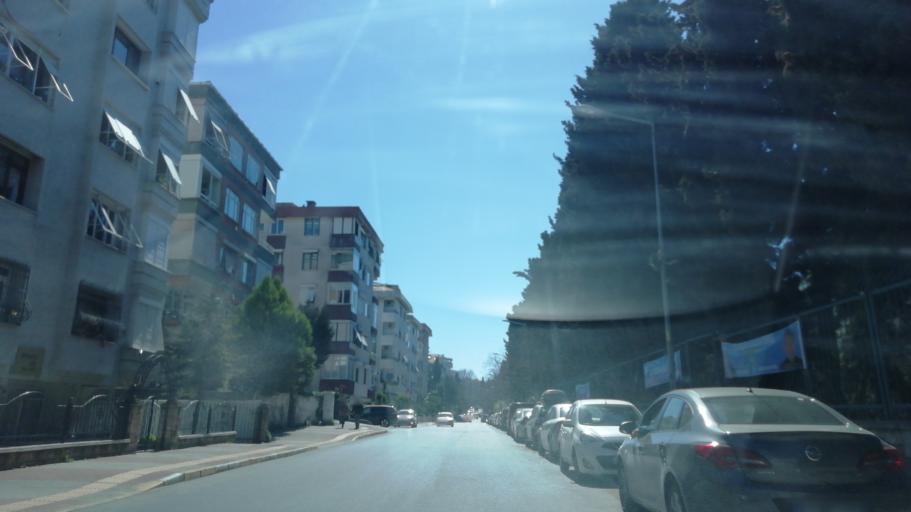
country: TR
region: Istanbul
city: Bahcelievler
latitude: 40.9870
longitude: 28.8660
